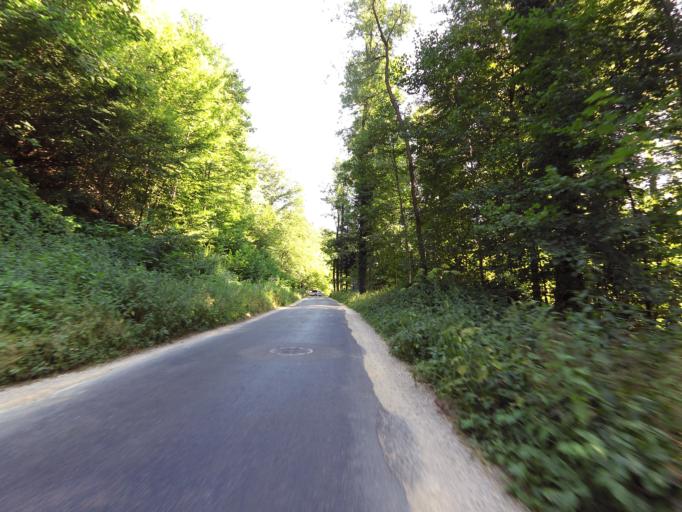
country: CH
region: Aargau
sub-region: Bezirk Lenzburg
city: Staufen
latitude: 47.3722
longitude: 8.1735
